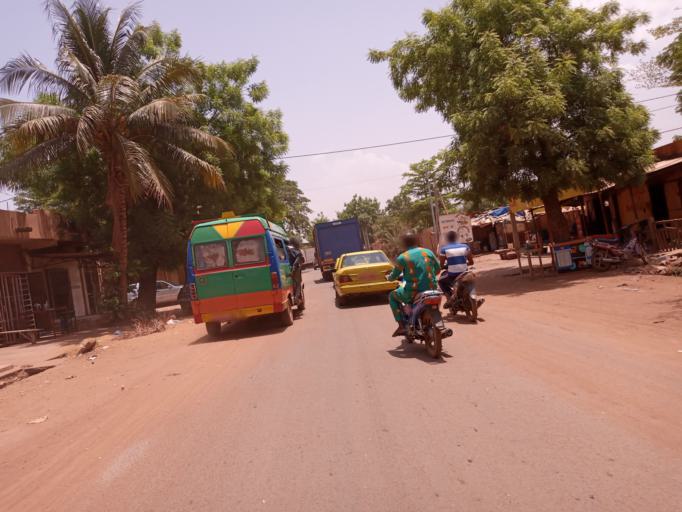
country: ML
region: Bamako
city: Bamako
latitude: 12.6469
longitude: -7.9794
